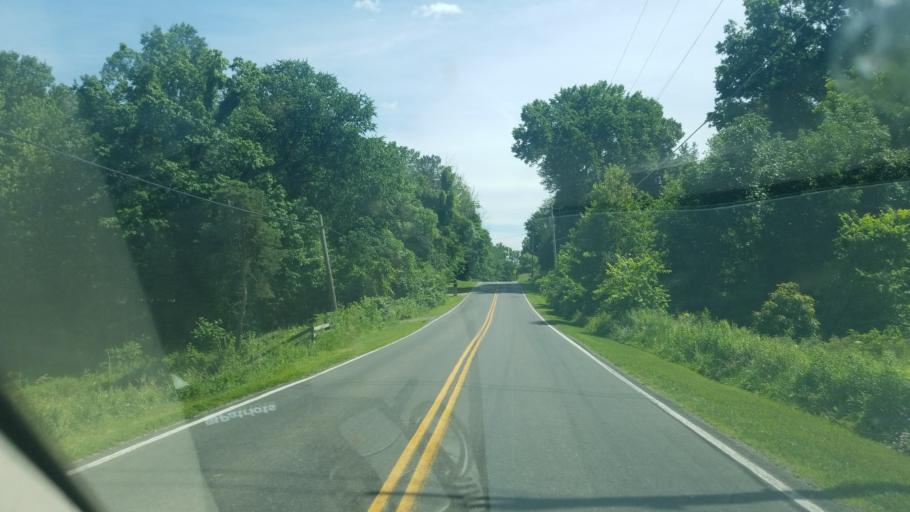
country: US
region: Ohio
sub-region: Stark County
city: Brewster
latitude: 40.7252
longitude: -81.5734
